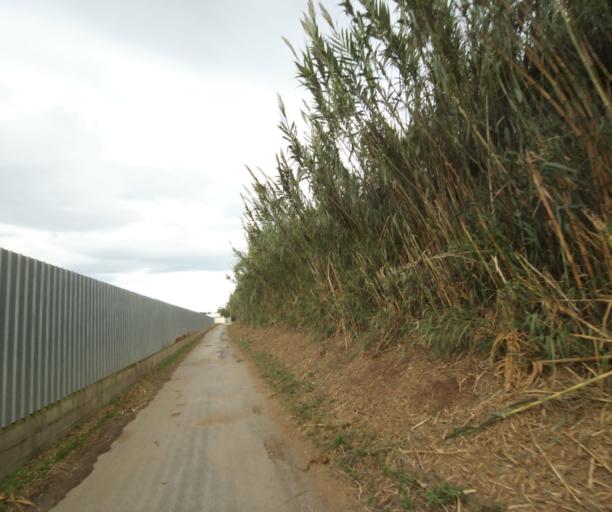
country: FR
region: Languedoc-Roussillon
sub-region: Departement des Pyrenees-Orientales
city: Argelers
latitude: 42.5824
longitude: 3.0298
